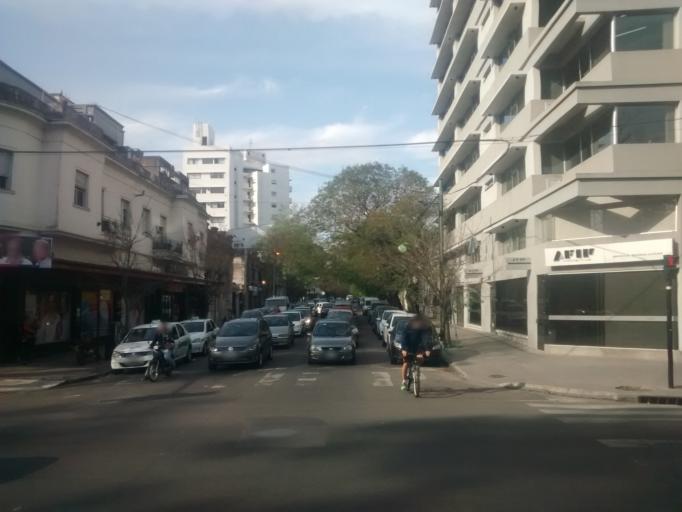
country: AR
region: Buenos Aires
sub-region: Partido de La Plata
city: La Plata
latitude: -34.9201
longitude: -57.9427
